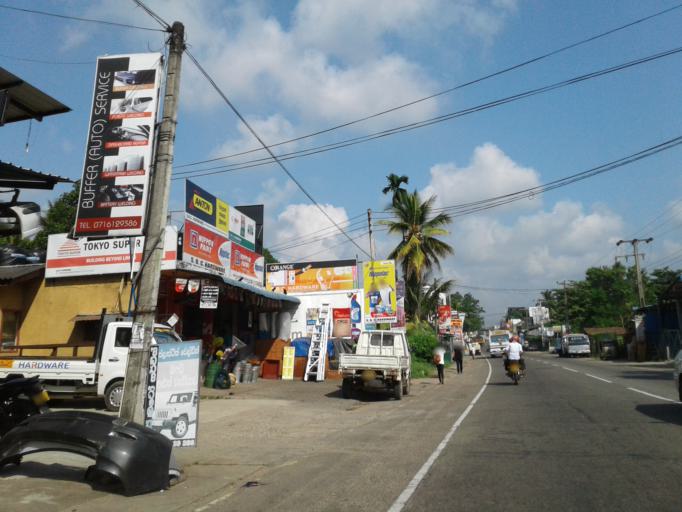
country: LK
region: Western
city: Battaramulla South
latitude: 6.9000
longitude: 79.9576
